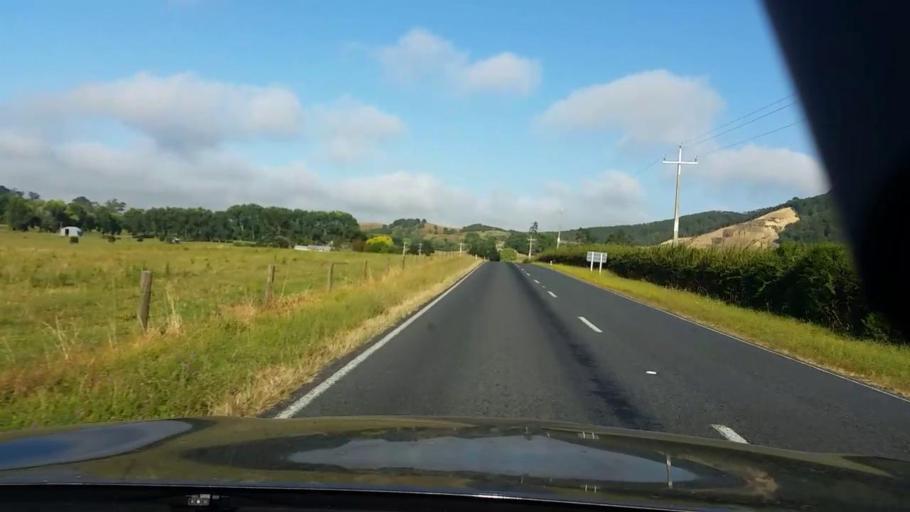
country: NZ
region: Waikato
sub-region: Hamilton City
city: Hamilton
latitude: -37.5922
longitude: 175.3734
